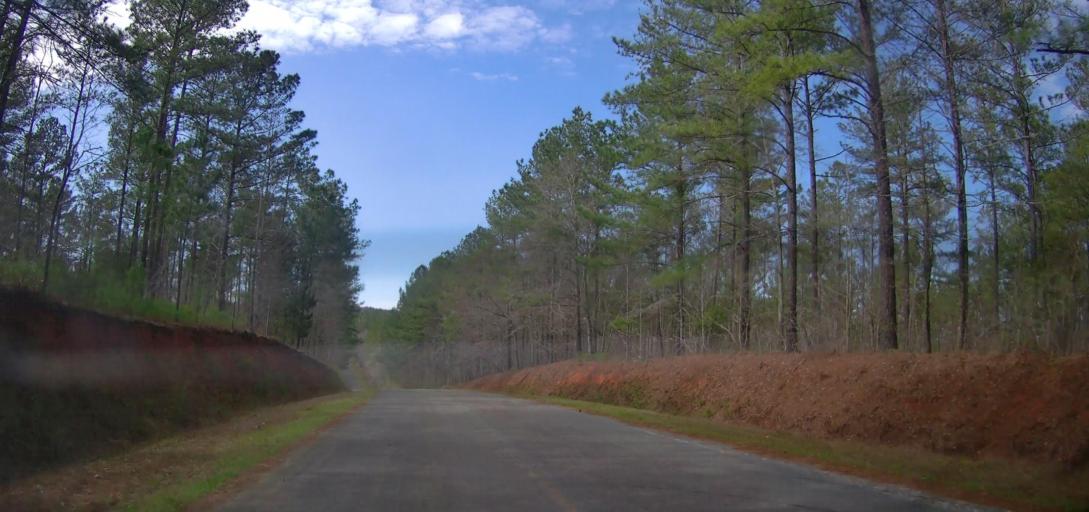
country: US
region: Georgia
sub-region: Monroe County
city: Forsyth
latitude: 33.0373
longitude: -83.8840
